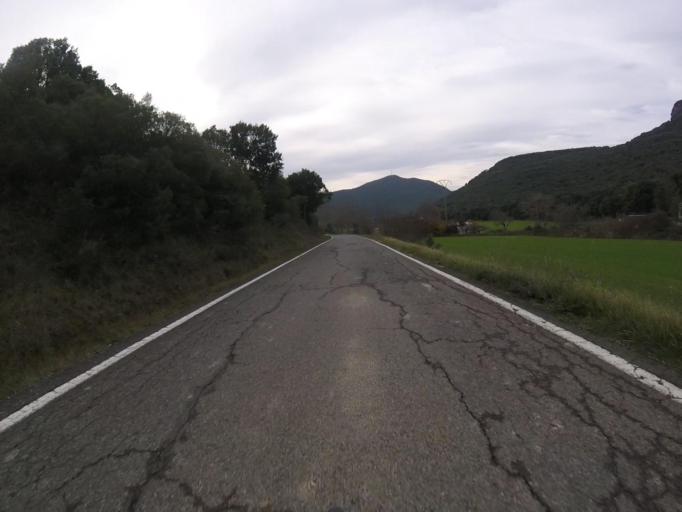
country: ES
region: Navarre
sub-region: Provincia de Navarra
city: Estella
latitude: 42.7062
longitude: -2.0516
